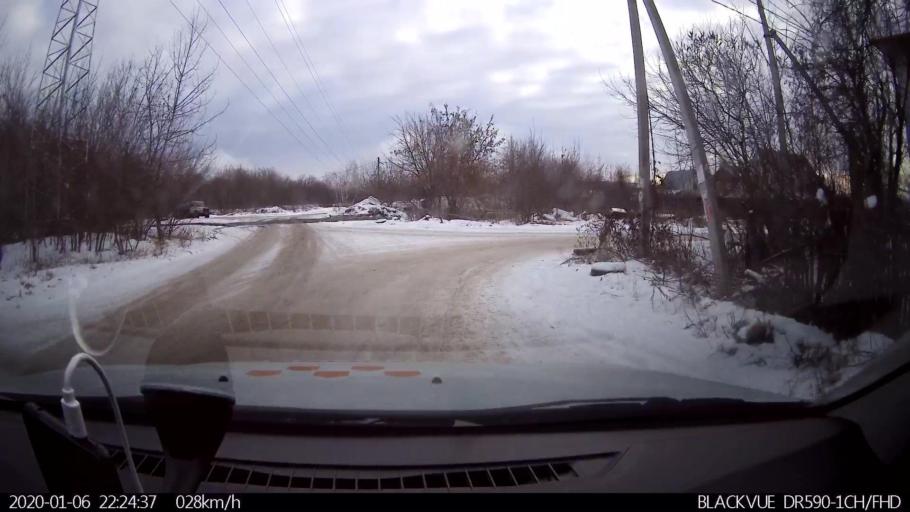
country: RU
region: Nizjnij Novgorod
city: Burevestnik
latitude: 56.2270
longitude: 43.8446
